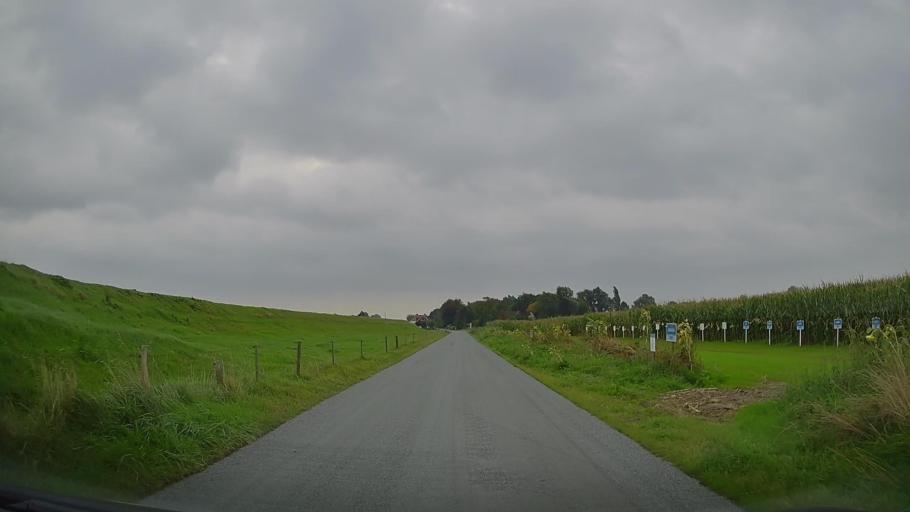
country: DE
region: Lower Saxony
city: Neuhaus an der Oste
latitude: 53.8200
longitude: 9.0267
